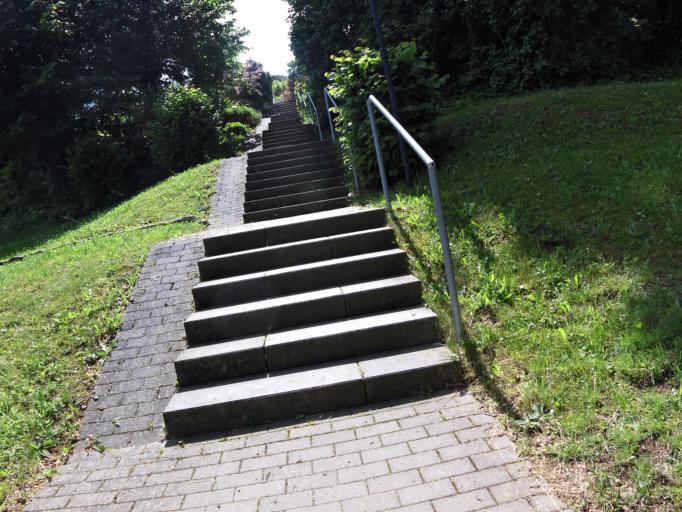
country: DE
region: Bavaria
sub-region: Regierungsbezirk Unterfranken
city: Hochberg
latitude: 49.7911
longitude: 9.9070
